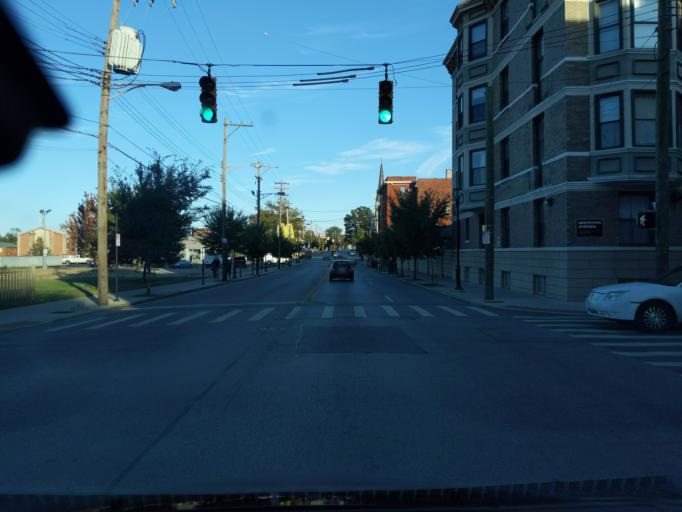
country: US
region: Kentucky
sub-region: Campbell County
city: Dayton
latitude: 39.1257
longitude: -84.4864
